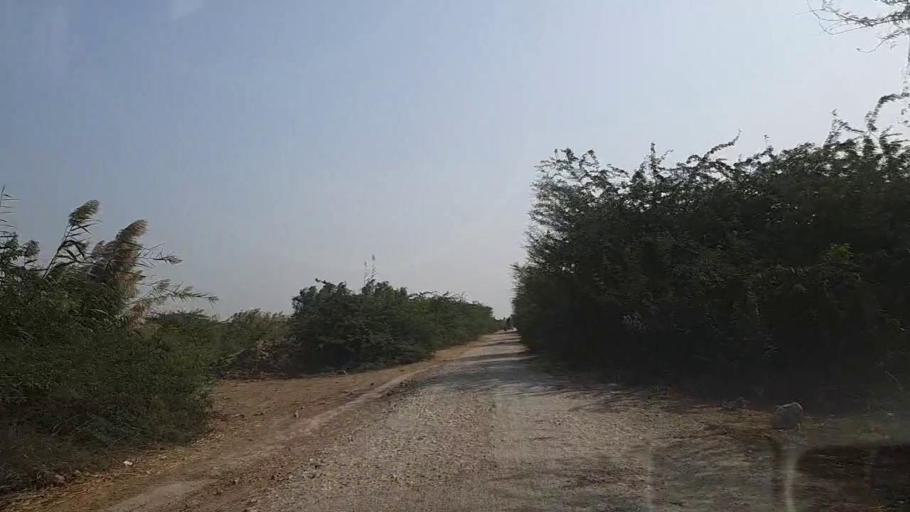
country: PK
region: Sindh
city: Keti Bandar
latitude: 24.2478
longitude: 67.6330
